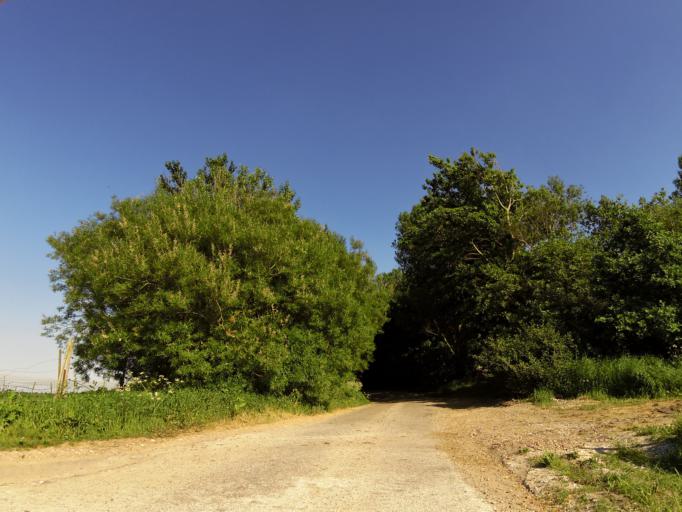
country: DK
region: Central Jutland
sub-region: Holstebro Kommune
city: Vinderup
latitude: 56.4662
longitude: 8.7101
